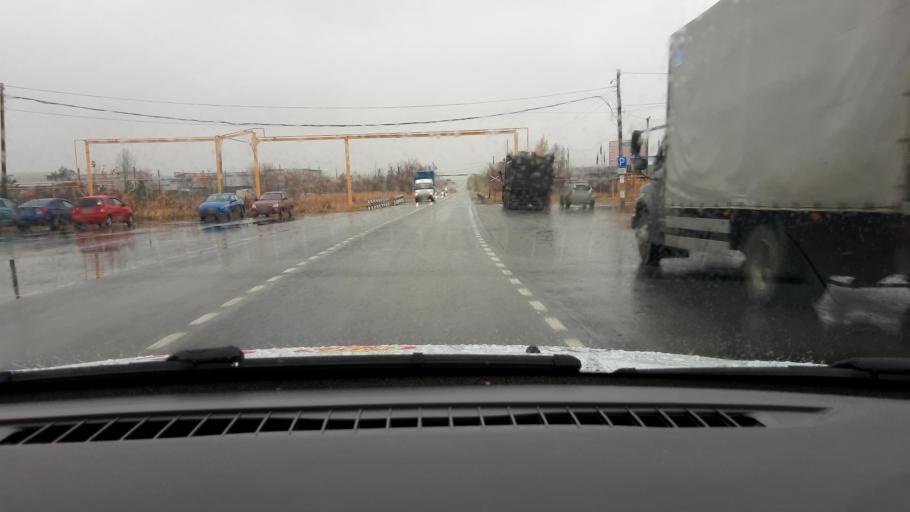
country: RU
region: Nizjnij Novgorod
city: Babino
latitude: 56.2579
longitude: 43.5939
